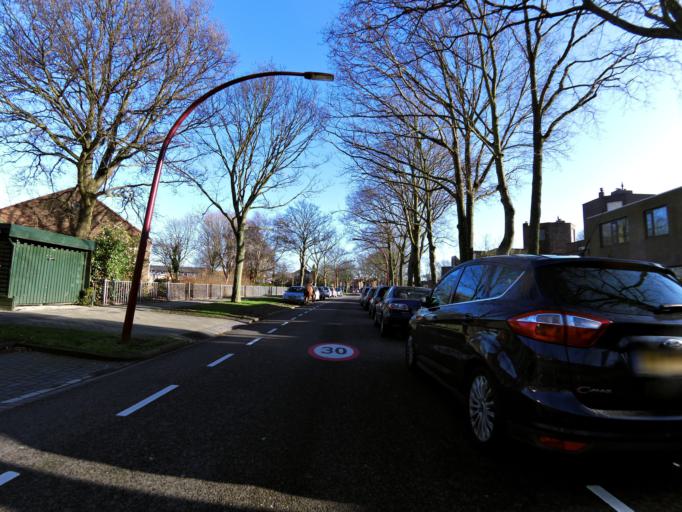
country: NL
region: South Holland
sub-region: Gemeente Hellevoetsluis
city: Nieuw-Helvoet
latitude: 51.8730
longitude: 4.0691
